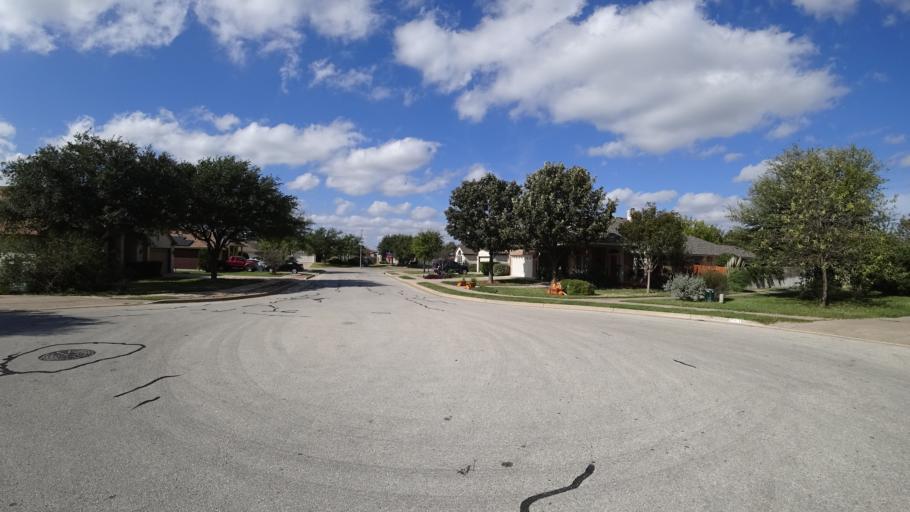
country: US
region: Texas
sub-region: Travis County
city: Windemere
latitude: 30.4709
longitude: -97.6548
